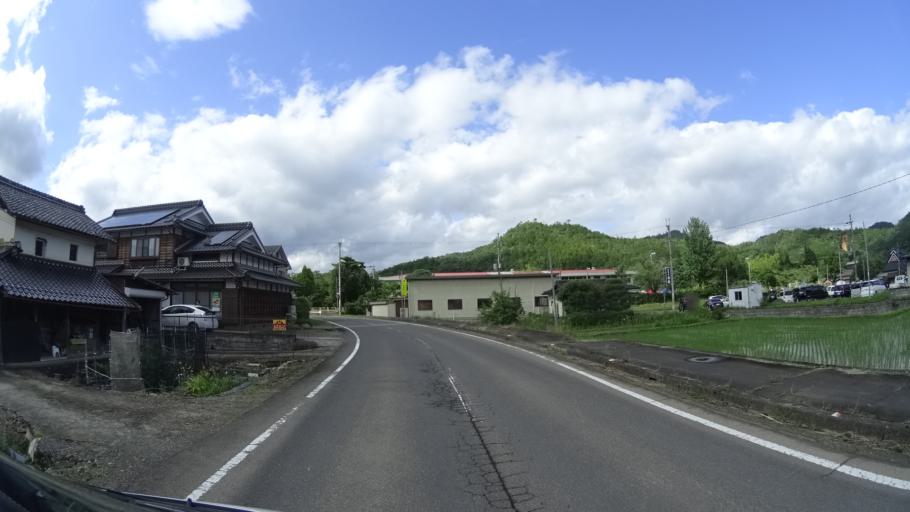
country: JP
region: Kyoto
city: Ayabe
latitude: 35.3698
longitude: 135.2407
